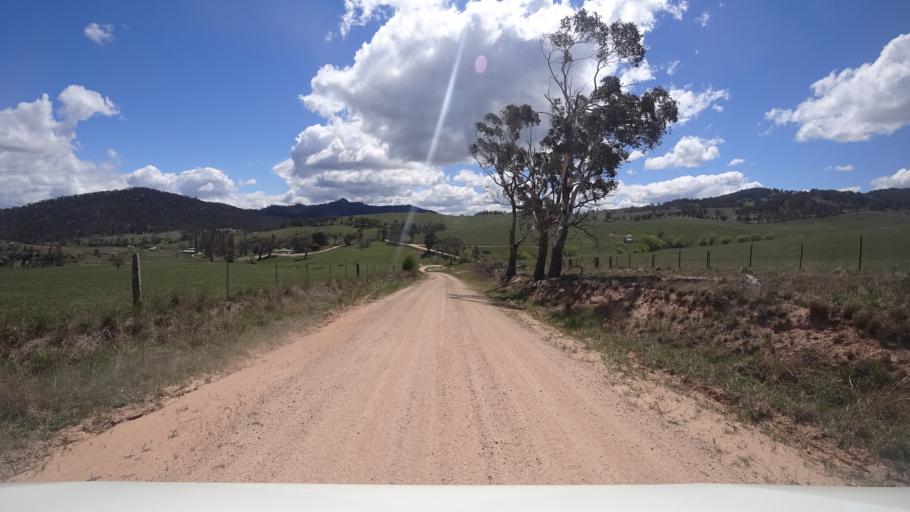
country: AU
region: New South Wales
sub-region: Oberon
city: Oberon
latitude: -33.5680
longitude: 149.9421
